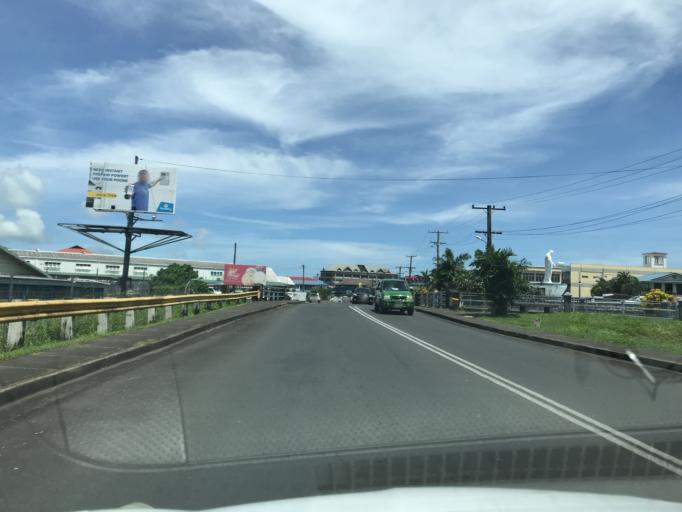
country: WS
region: Tuamasaga
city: Apia
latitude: -13.8331
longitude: -171.7664
